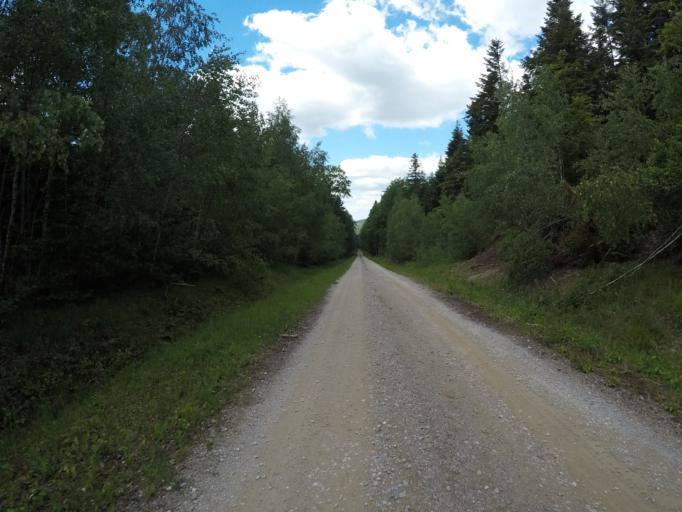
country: PL
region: Swietokrzyskie
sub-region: Powiat kielecki
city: Kostomloty Pierwsze
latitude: 50.9338
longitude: 20.6194
